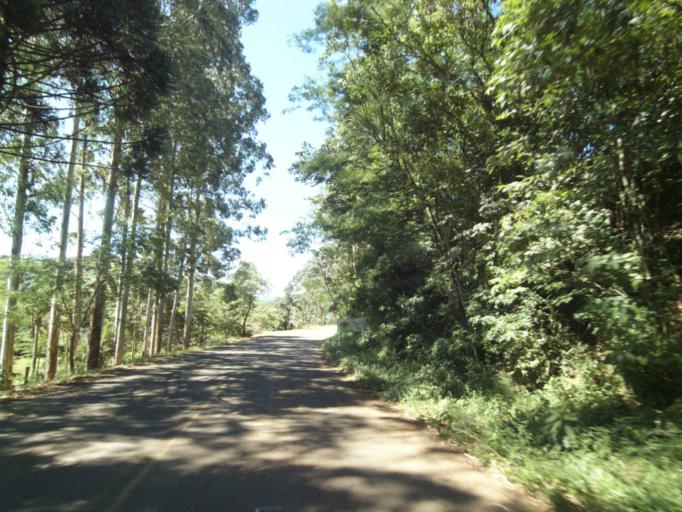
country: BR
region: Parana
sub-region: Ampere
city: Ampere
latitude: -26.1816
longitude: -53.3644
